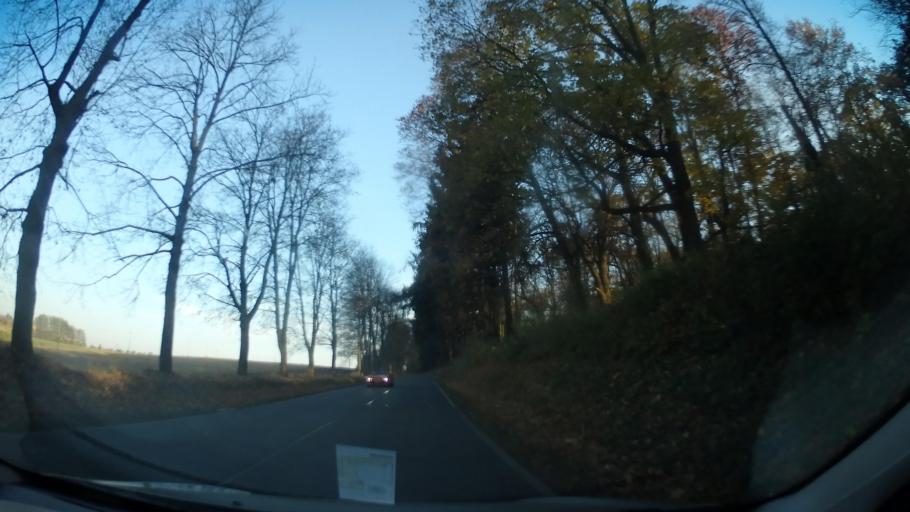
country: CZ
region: Central Bohemia
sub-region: Okres Benesov
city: Benesov
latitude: 49.7815
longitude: 14.6659
